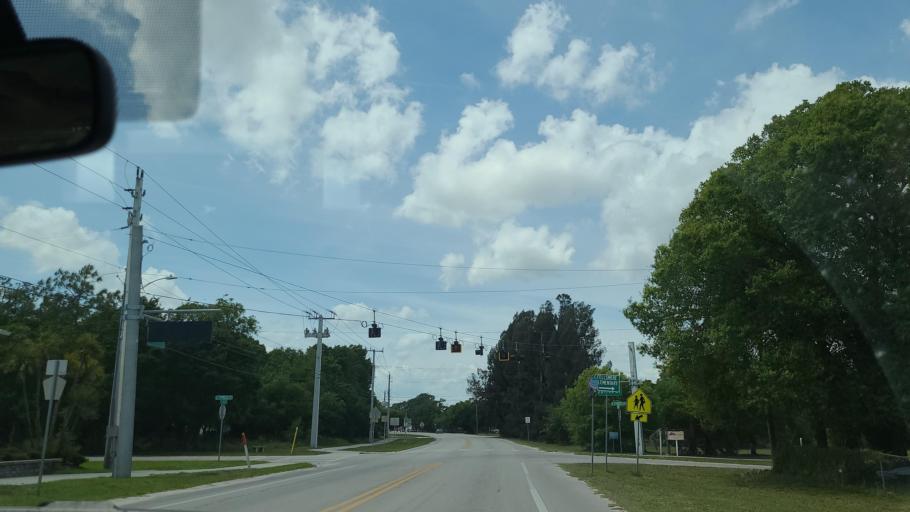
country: US
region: Florida
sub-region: Indian River County
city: Fellsmere
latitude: 27.7677
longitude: -80.6032
